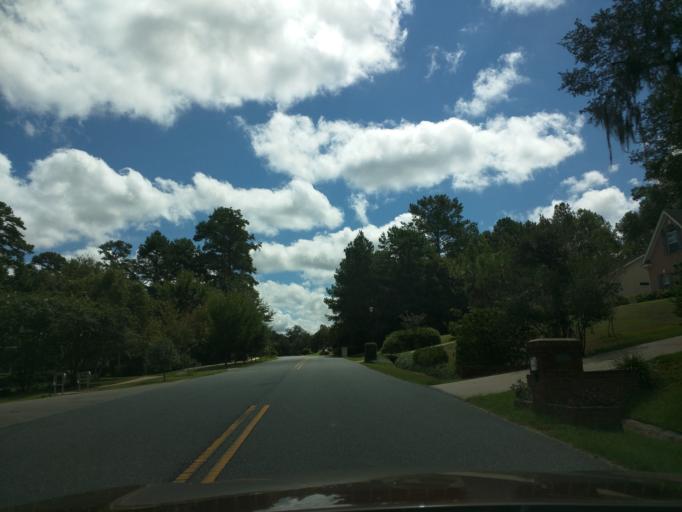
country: US
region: Florida
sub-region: Leon County
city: Tallahassee
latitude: 30.5697
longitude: -84.2615
